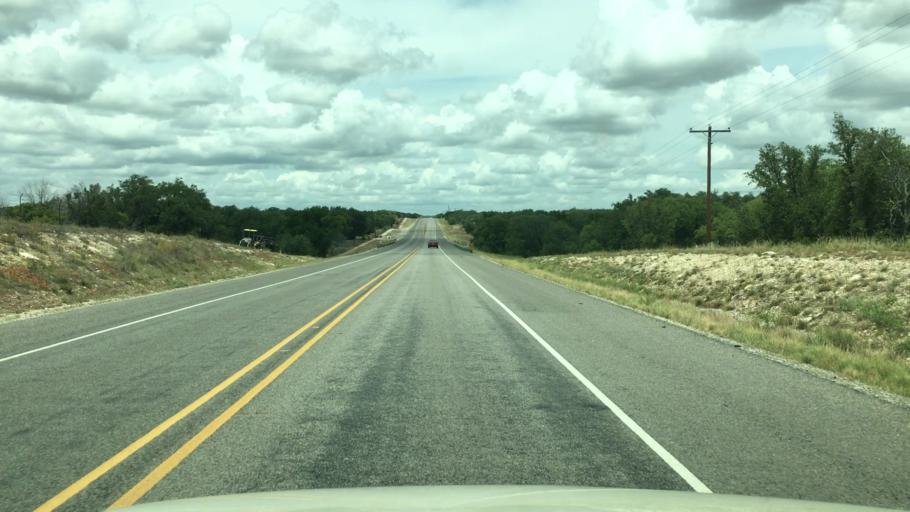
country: US
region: Texas
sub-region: McCulloch County
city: Brady
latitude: 31.0391
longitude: -99.2402
